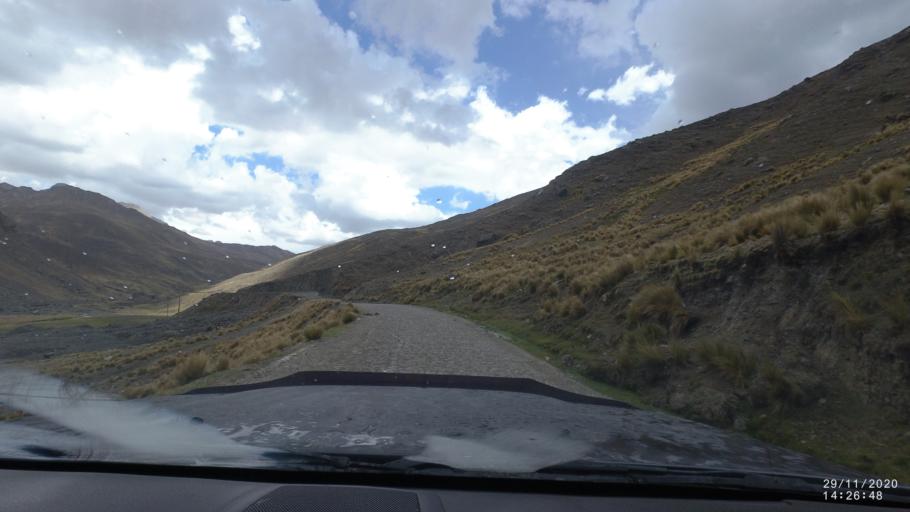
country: BO
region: Cochabamba
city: Sipe Sipe
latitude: -17.2587
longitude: -66.3686
